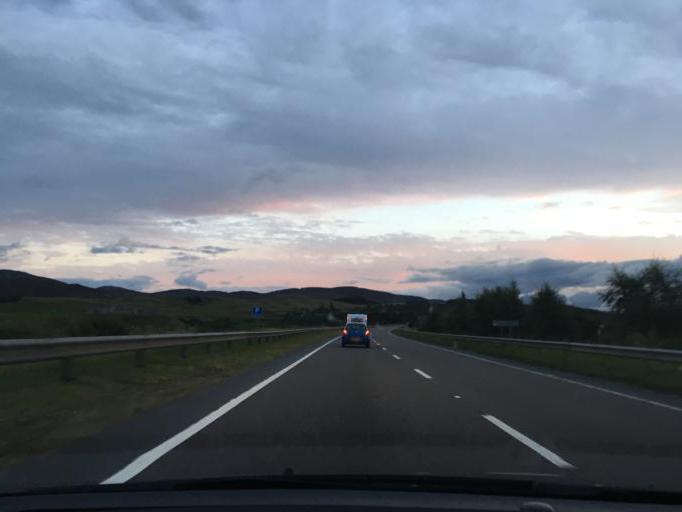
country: GB
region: Scotland
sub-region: Highland
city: Kingussie
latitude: 57.0779
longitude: -4.0401
